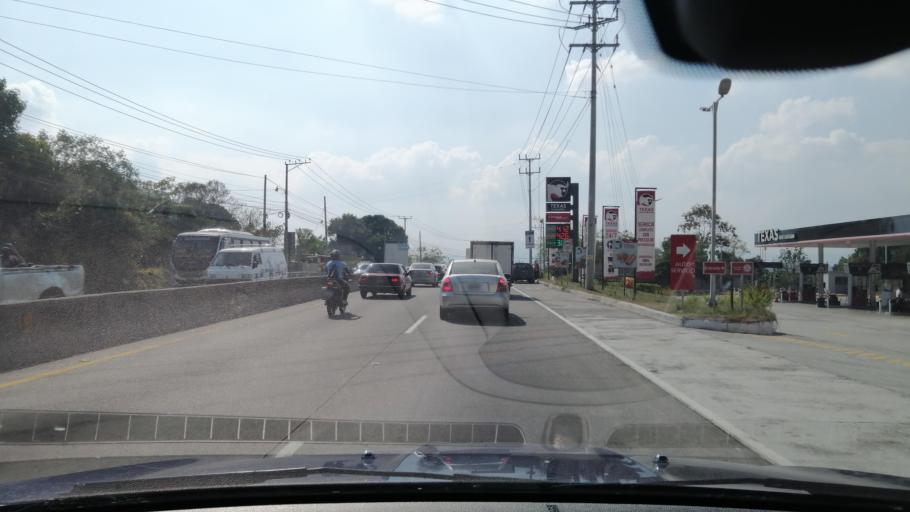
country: SV
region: San Salvador
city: Mejicanos
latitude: 13.7446
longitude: -89.2185
